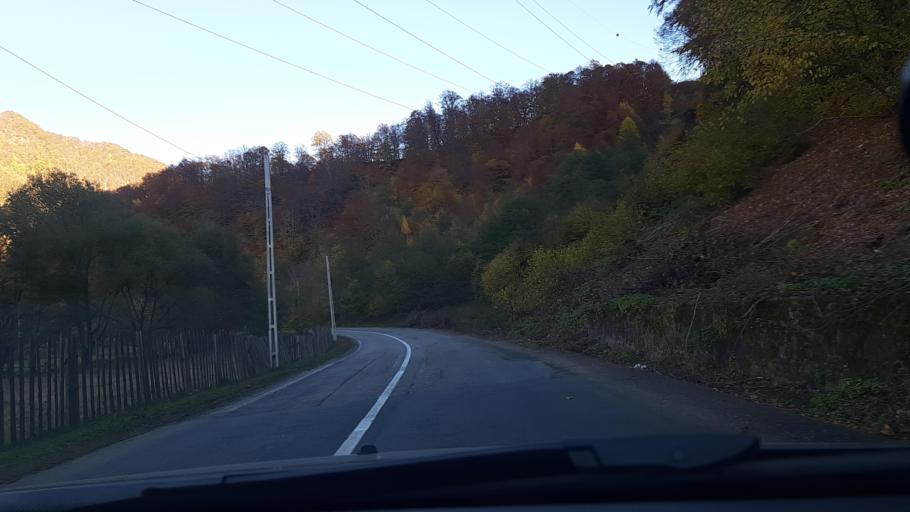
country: RO
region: Valcea
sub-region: Comuna Brezoi
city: Brezoi
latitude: 45.3472
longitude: 24.1481
